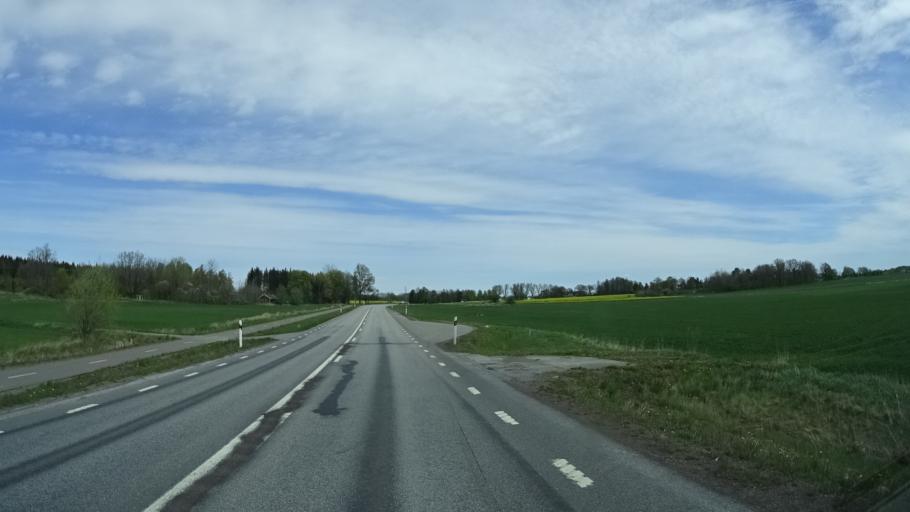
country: SE
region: OEstergoetland
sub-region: Linkopings Kommun
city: Vikingstad
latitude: 58.3703
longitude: 15.3889
